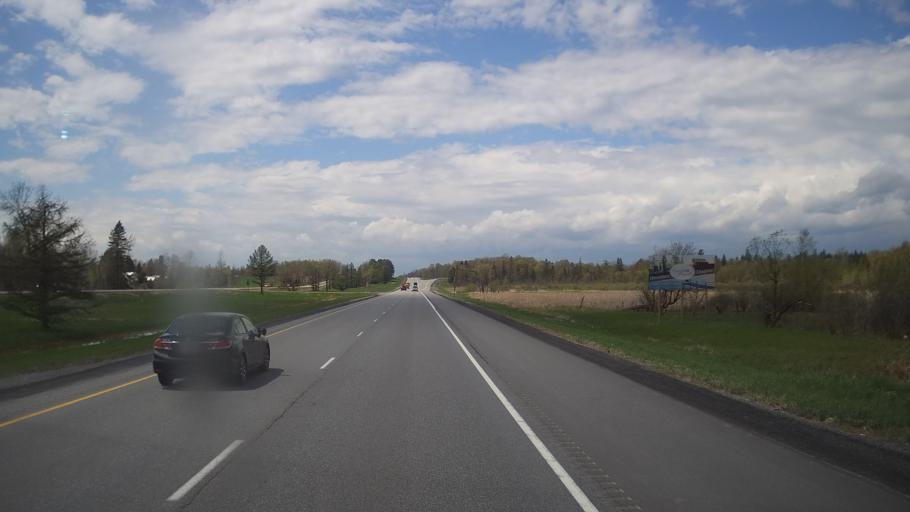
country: CA
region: Quebec
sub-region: Monteregie
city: Rigaud
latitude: 45.5448
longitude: -74.4113
